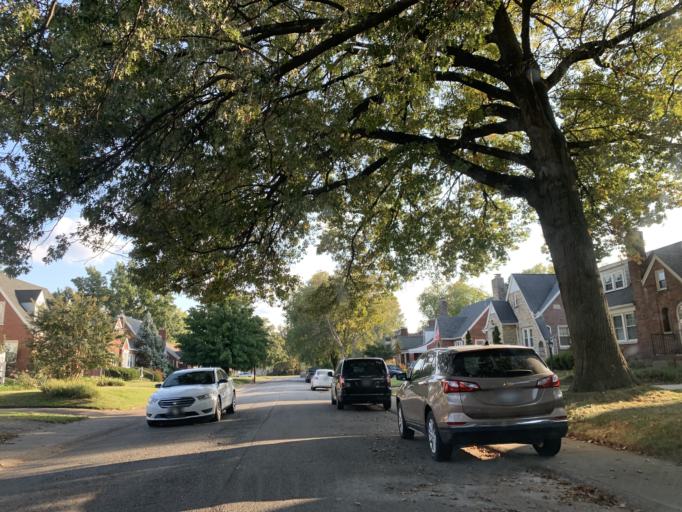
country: US
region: Kentucky
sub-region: Jefferson County
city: Audubon Park
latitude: 38.1885
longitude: -85.7628
